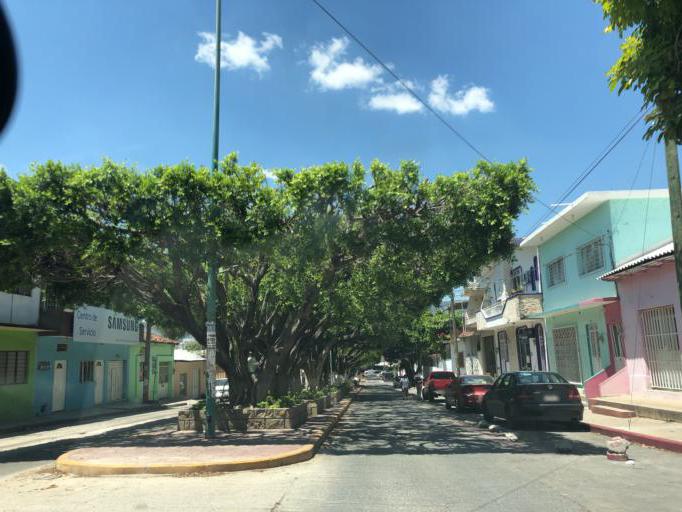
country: MX
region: Chiapas
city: Tuxtla Gutierrez
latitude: 16.7607
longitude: -93.1186
